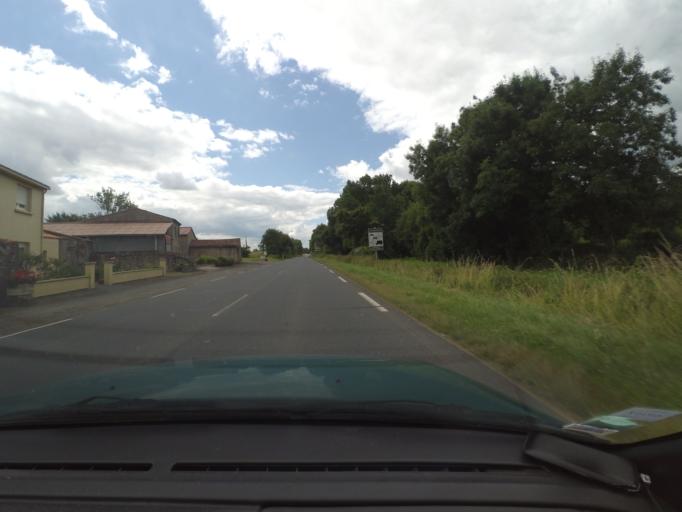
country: FR
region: Pays de la Loire
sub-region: Departement de la Loire-Atlantique
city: Mouzillon
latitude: 47.1200
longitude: -1.2828
